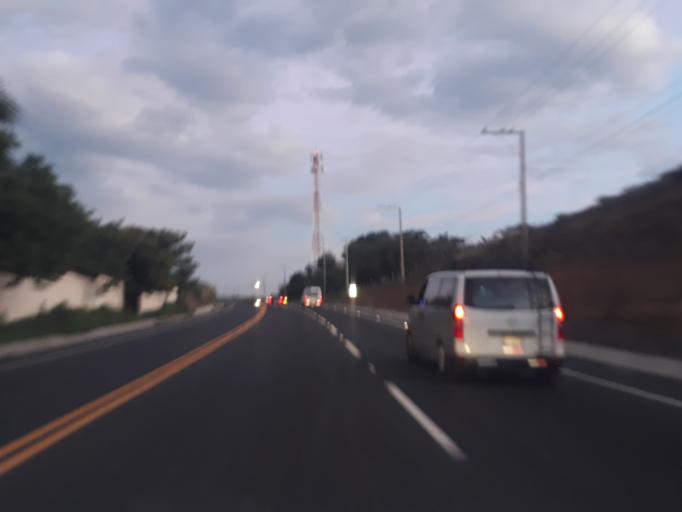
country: NI
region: Managua
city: El Crucero
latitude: 12.0014
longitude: -86.3189
